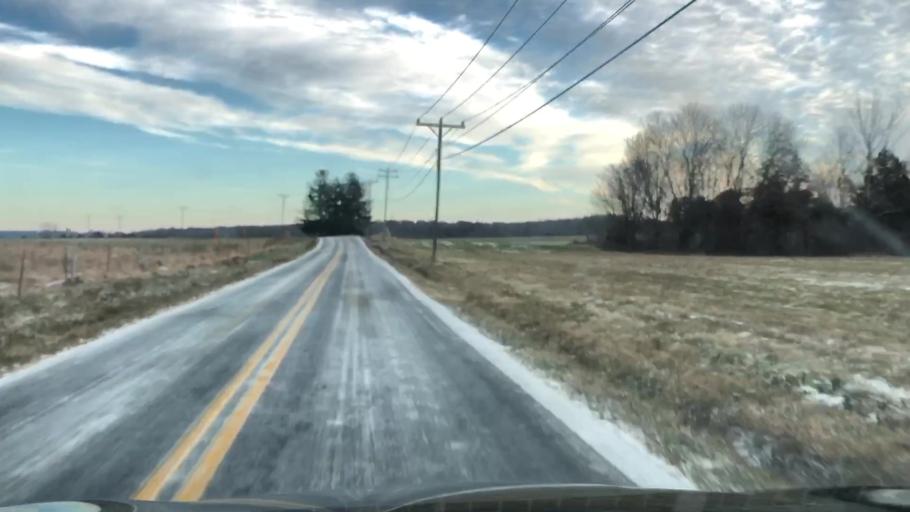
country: US
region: Virginia
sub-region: Prince William County
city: Nokesville
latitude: 38.6602
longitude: -77.6750
